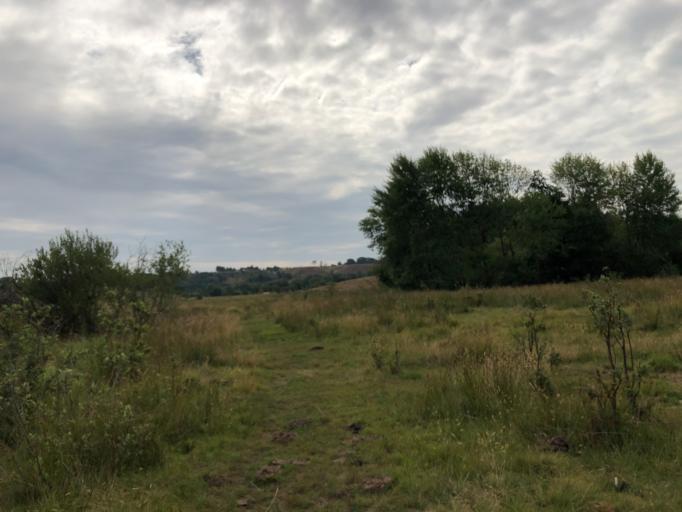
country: DK
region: South Denmark
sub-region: Vejle Kommune
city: Egtved
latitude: 55.6515
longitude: 9.2757
